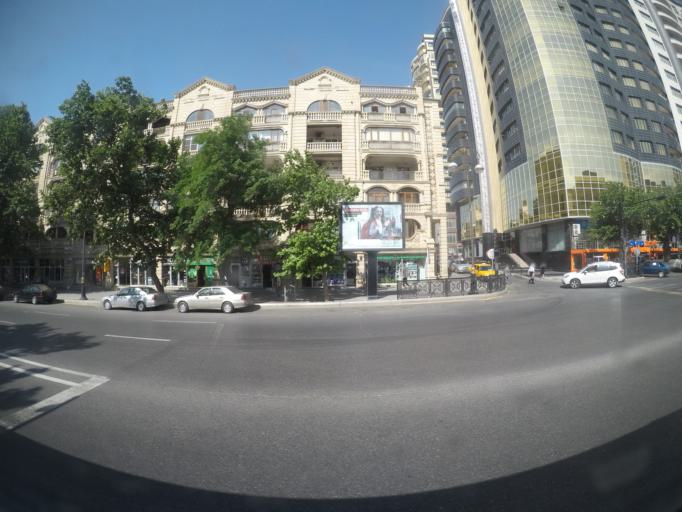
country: AZ
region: Baki
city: Badamdar
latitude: 40.3777
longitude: 49.8319
